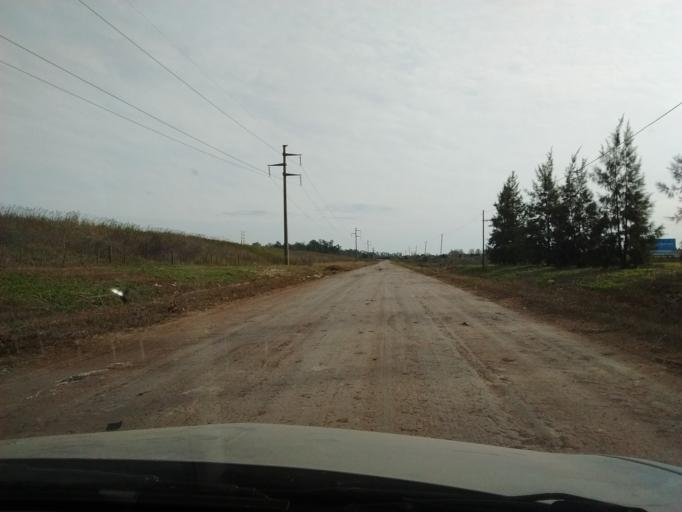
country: AR
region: Santa Fe
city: Funes
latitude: -32.9424
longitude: -60.8103
